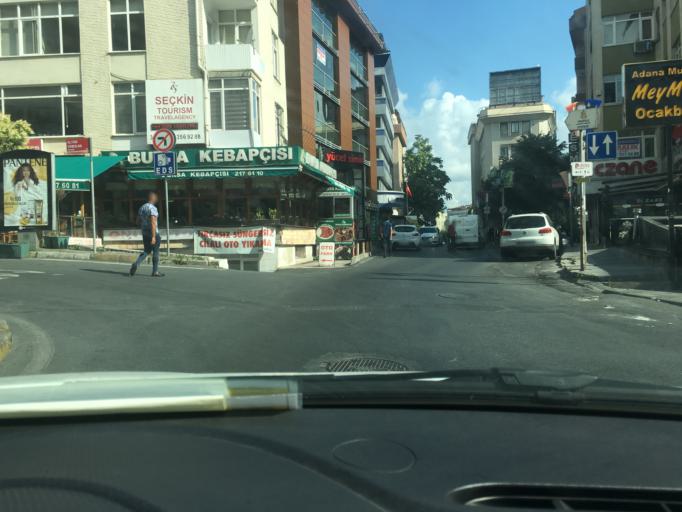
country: TR
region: Istanbul
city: Sisli
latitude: 41.0675
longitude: 29.0033
